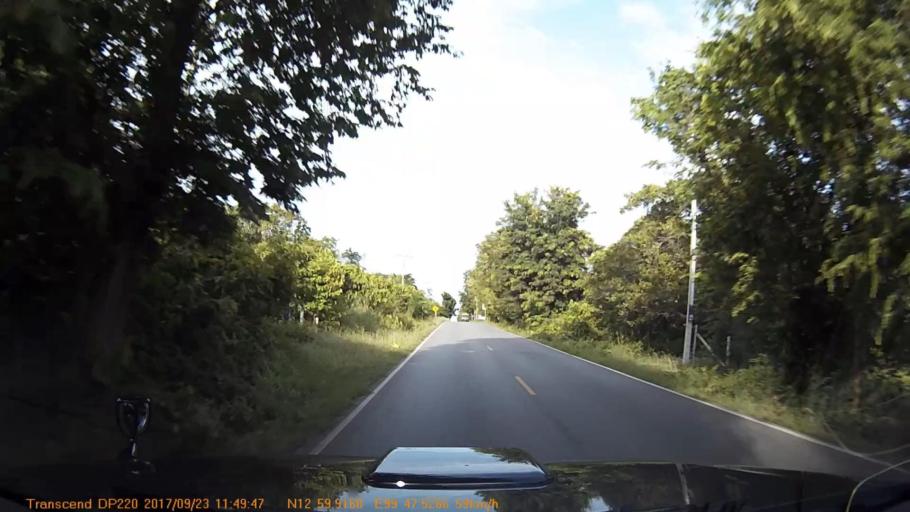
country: TH
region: Phetchaburi
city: Tha Yang
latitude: 12.9986
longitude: 99.7922
